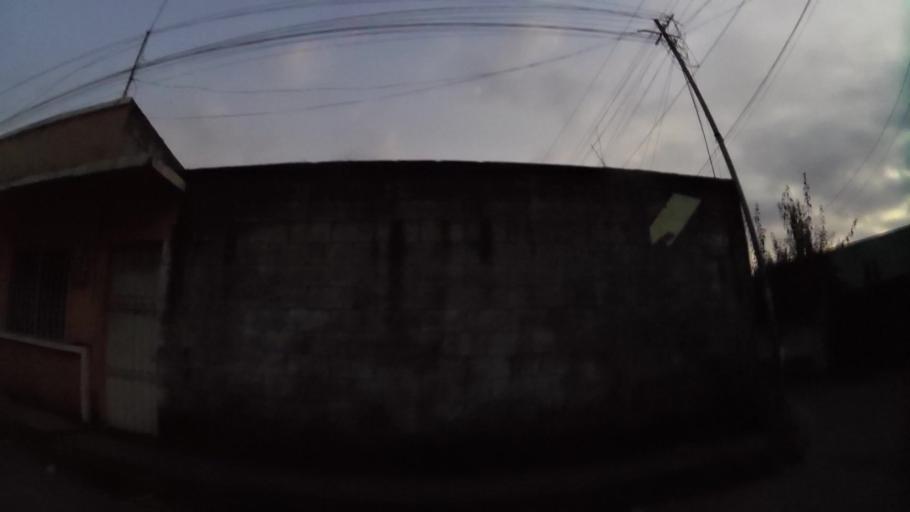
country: GT
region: Retalhuleu
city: San Felipe
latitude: 14.6227
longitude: -91.5980
